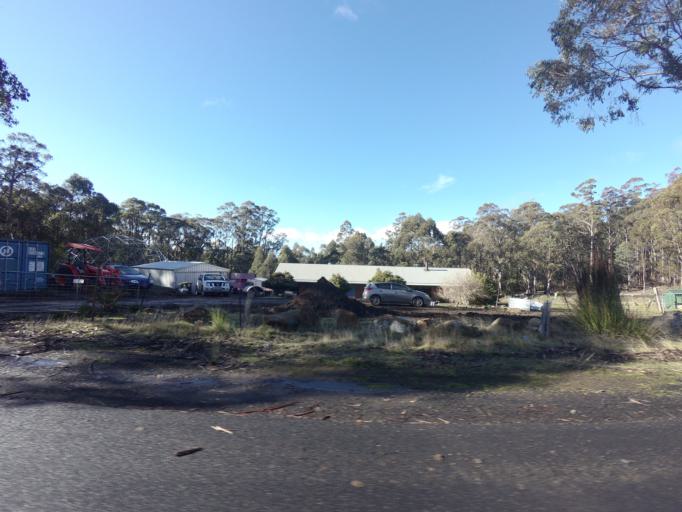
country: AU
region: Tasmania
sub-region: Glenorchy
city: Berriedale
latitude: -42.8386
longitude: 147.1585
